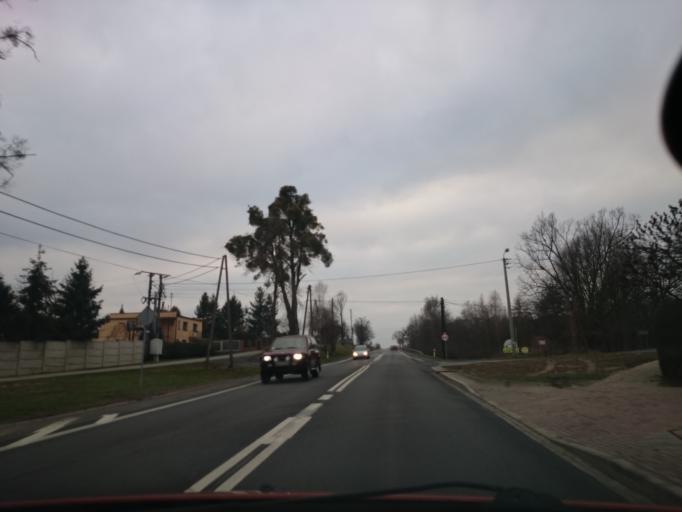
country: PL
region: Opole Voivodeship
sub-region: Powiat opolski
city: Niemodlin
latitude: 50.6413
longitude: 17.6095
